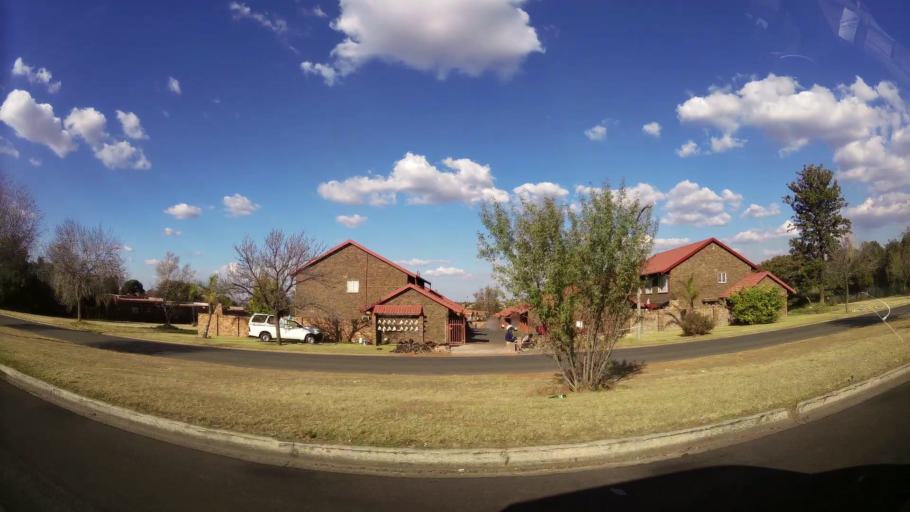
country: ZA
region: Mpumalanga
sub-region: Nkangala District Municipality
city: Witbank
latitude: -25.8849
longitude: 29.2339
